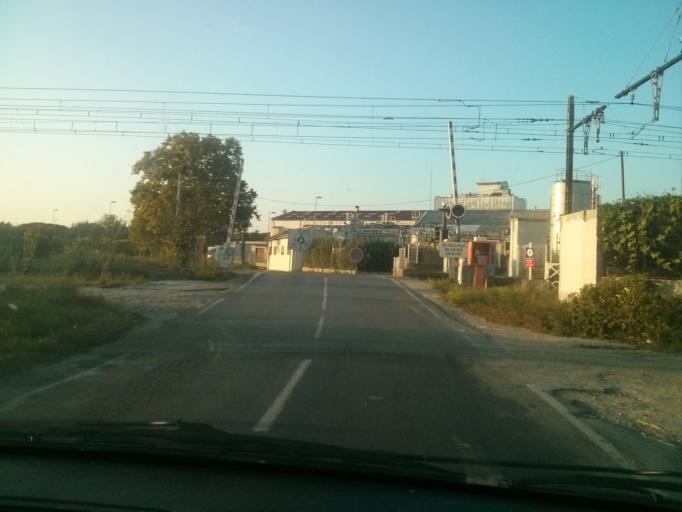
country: FR
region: Languedoc-Roussillon
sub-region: Departement du Gard
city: Mus
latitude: 43.7263
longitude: 4.1934
